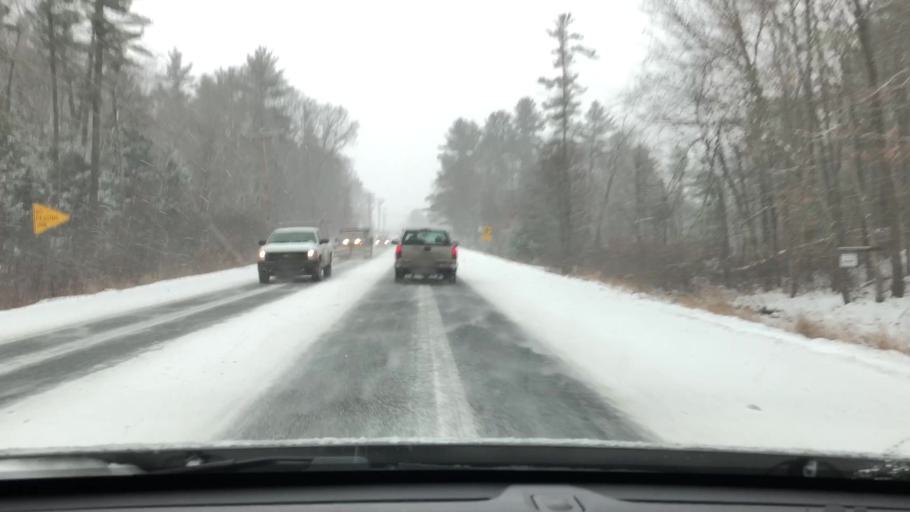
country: US
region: New Hampshire
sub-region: Strafford County
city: Lee
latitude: 43.1710
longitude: -71.0039
